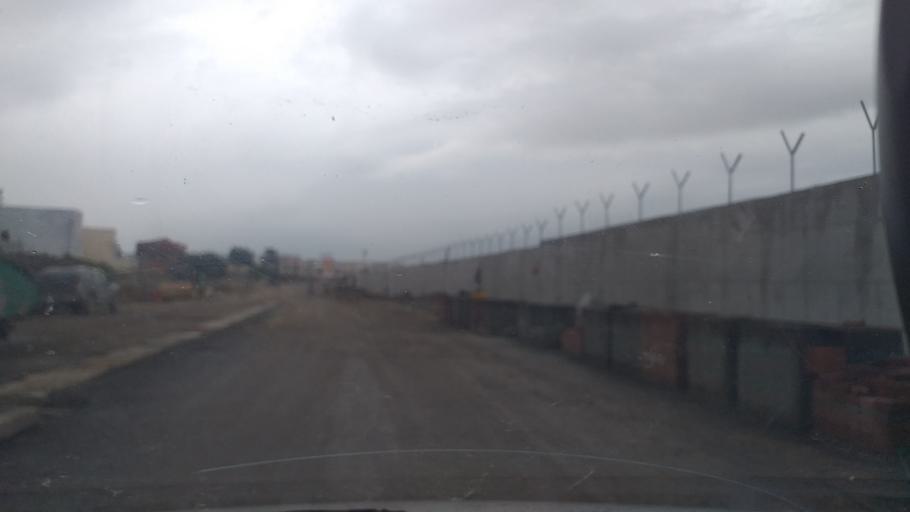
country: TN
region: Ariana
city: Ariana
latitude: 36.8660
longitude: 10.2271
